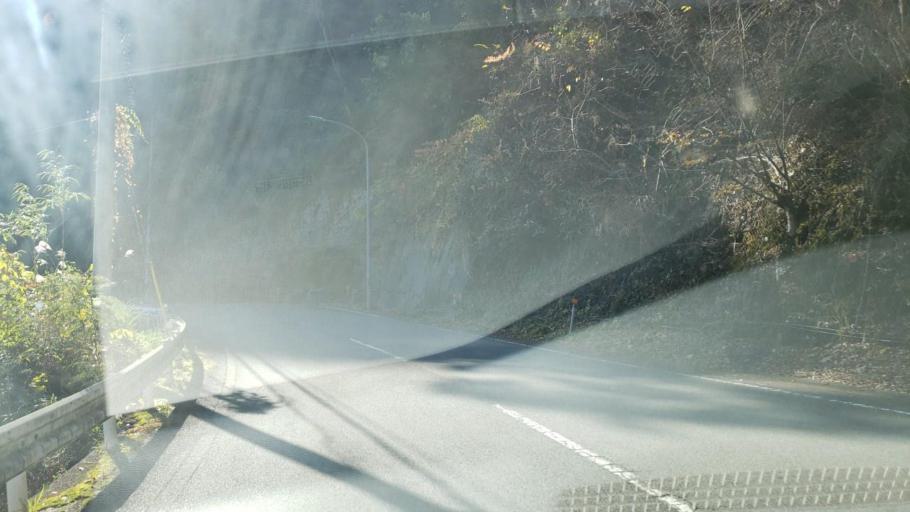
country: JP
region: Tokushima
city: Wakimachi
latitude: 34.0087
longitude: 134.0319
